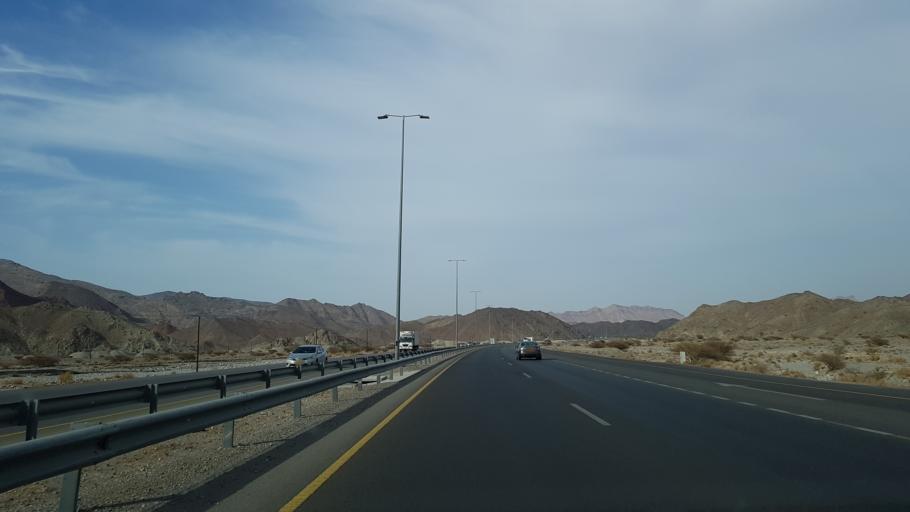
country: OM
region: Muhafazat ad Dakhiliyah
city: Bidbid
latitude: 23.3871
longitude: 58.0600
